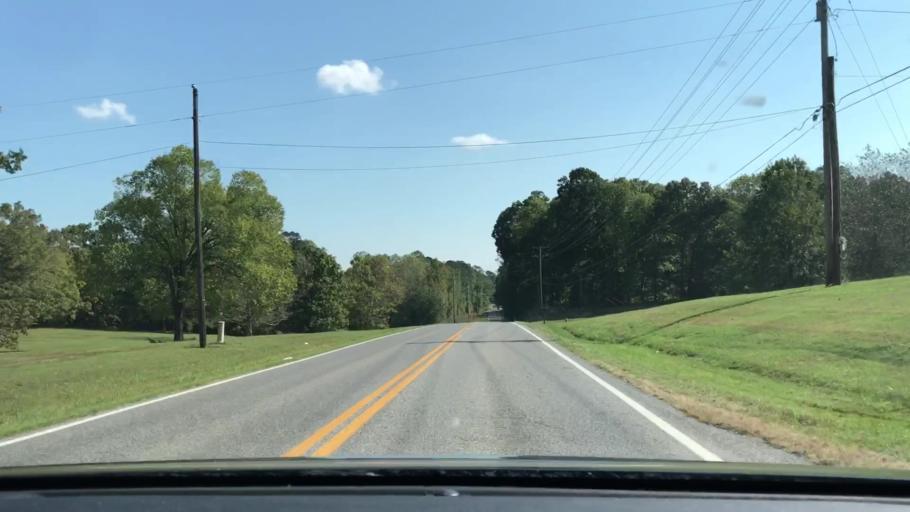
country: US
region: Kentucky
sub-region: Marshall County
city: Benton
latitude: 36.7645
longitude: -88.2522
